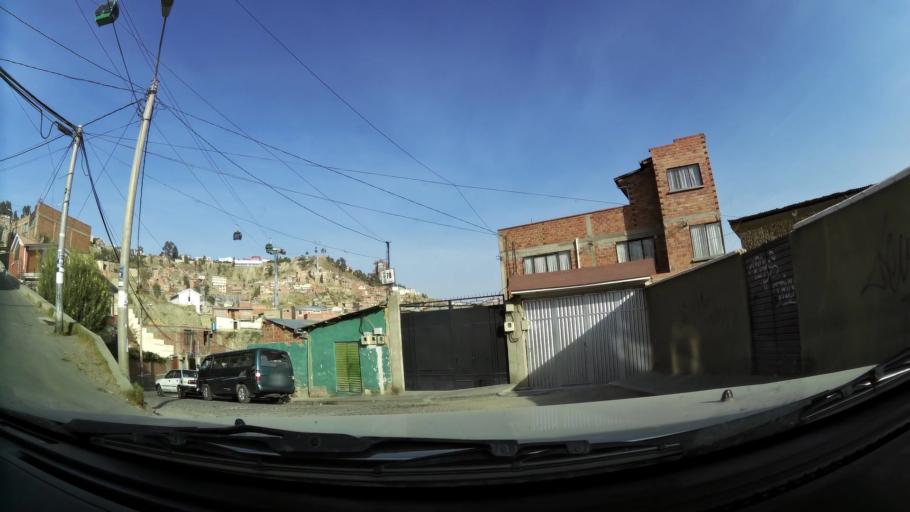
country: BO
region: La Paz
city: La Paz
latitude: -16.5310
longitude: -68.0961
